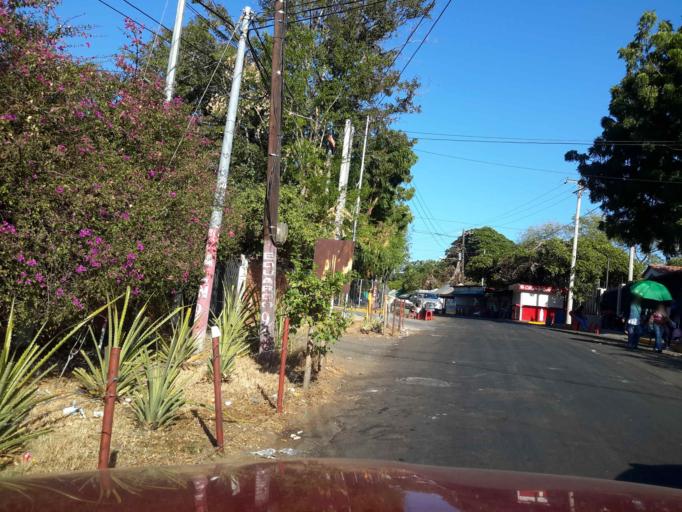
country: NI
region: Managua
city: Managua
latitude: 12.1252
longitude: -86.2679
